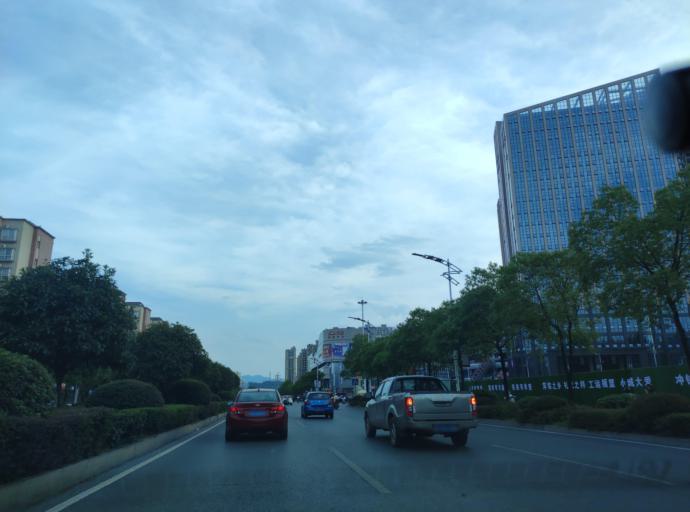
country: CN
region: Jiangxi Sheng
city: Pingxiang
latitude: 27.6383
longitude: 113.8703
